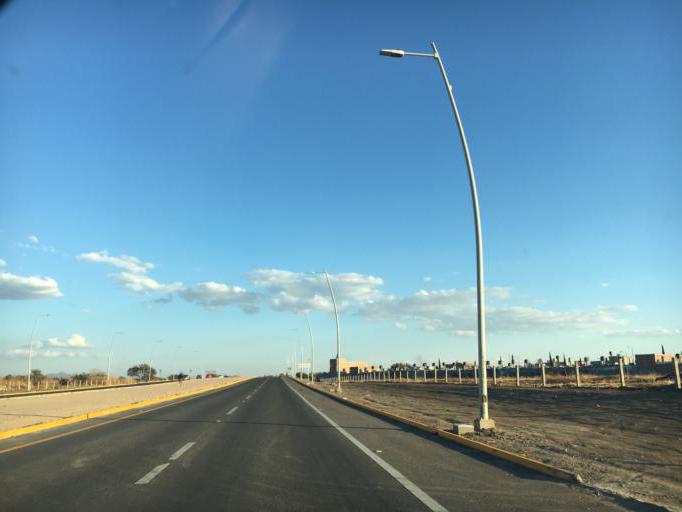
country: MX
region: Guanajuato
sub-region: Leon
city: Fraccionamiento Paraiso Real
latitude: 21.1021
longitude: -101.5758
